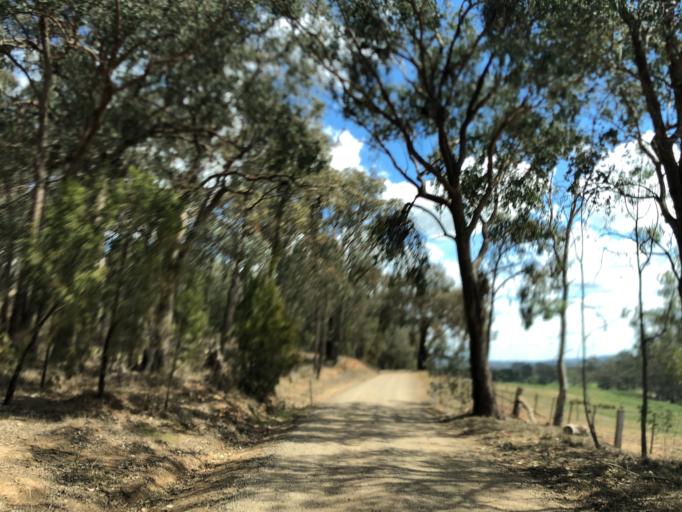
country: AU
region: Victoria
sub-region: Benalla
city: Benalla
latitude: -36.7297
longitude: 146.1242
